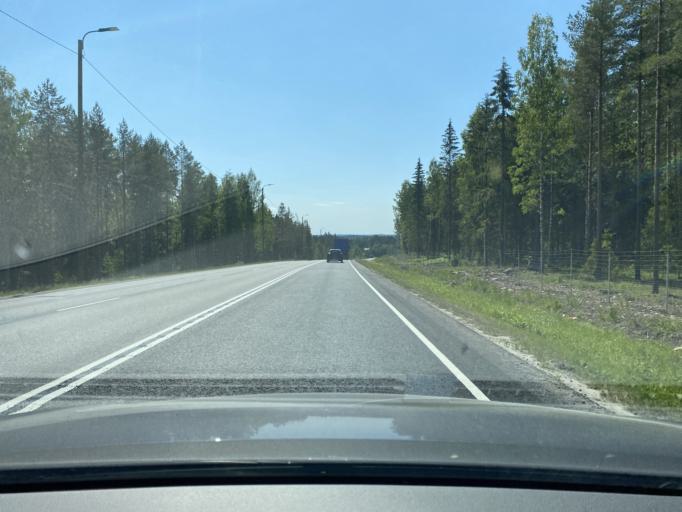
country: FI
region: Pirkanmaa
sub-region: Lounais-Pirkanmaa
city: Mouhijaervi
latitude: 61.3740
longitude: 23.1444
